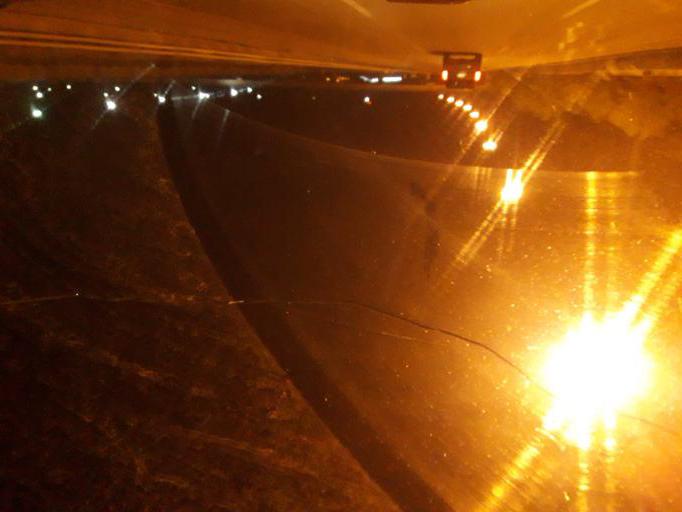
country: SA
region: Makkah
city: Mecca
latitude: 21.3279
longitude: 39.9842
